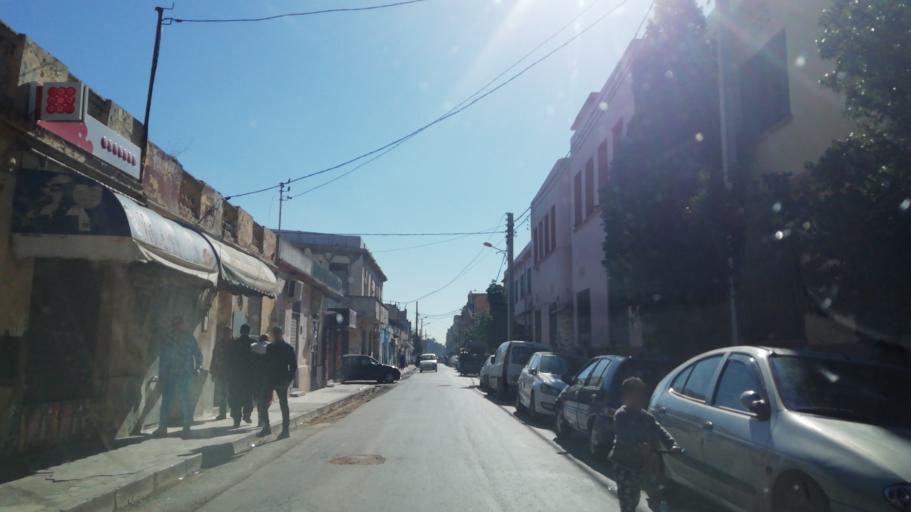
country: DZ
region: Oran
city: Oran
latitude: 35.6881
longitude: -0.6401
